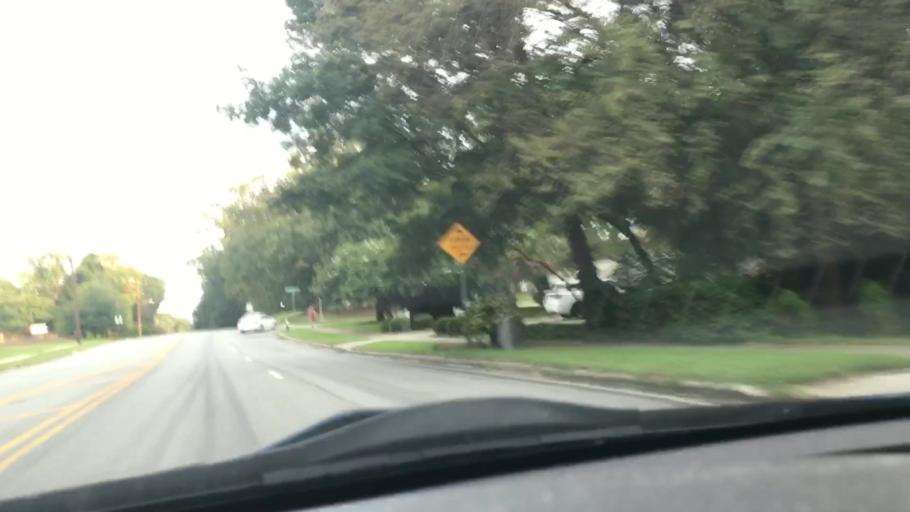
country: US
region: North Carolina
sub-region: Guilford County
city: Greensboro
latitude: 36.0804
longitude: -79.8270
